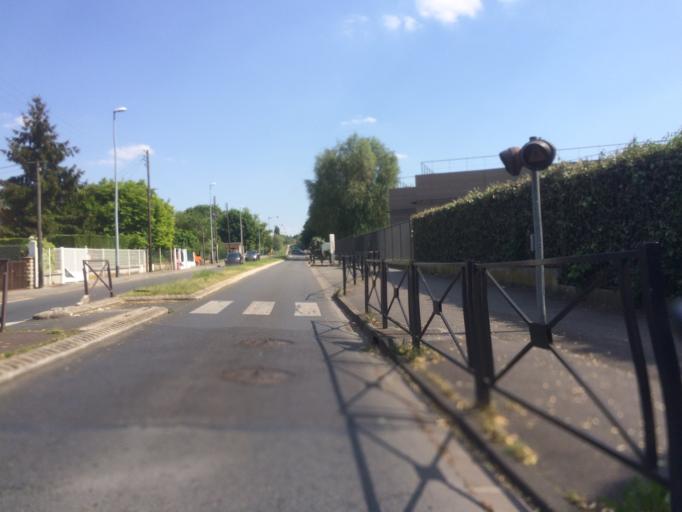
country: FR
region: Ile-de-France
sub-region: Departement de l'Essonne
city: Savigny-sur-Orge
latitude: 48.6782
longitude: 2.3597
